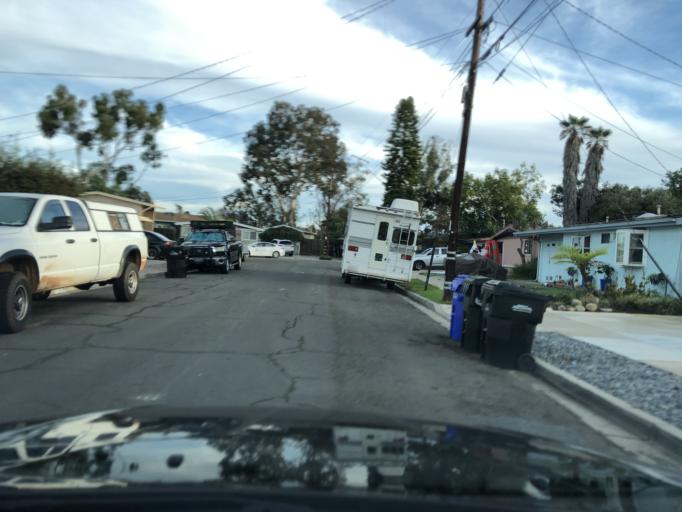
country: US
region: California
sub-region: San Diego County
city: La Jolla
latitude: 32.8302
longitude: -117.1933
